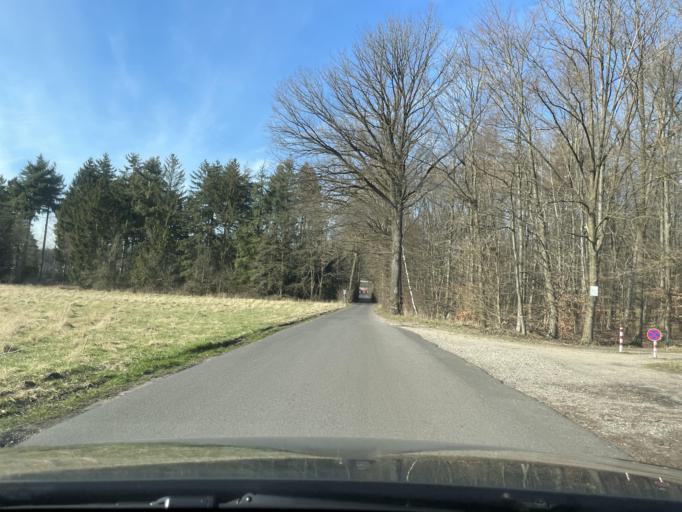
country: DE
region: North Rhine-Westphalia
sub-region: Regierungsbezirk Dusseldorf
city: Bruggen
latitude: 51.2387
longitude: 6.1519
